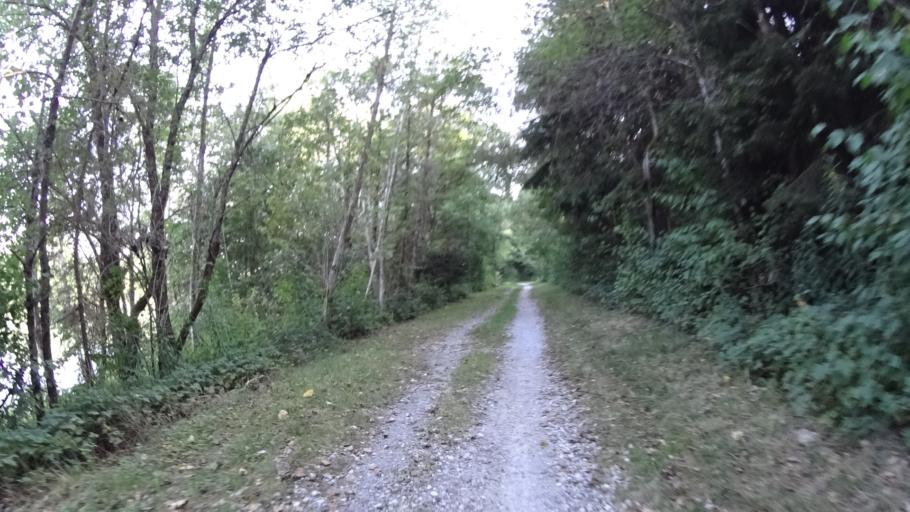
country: AT
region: Carinthia
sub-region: Politischer Bezirk Villach Land
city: Rosegg
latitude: 46.5743
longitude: 14.0213
